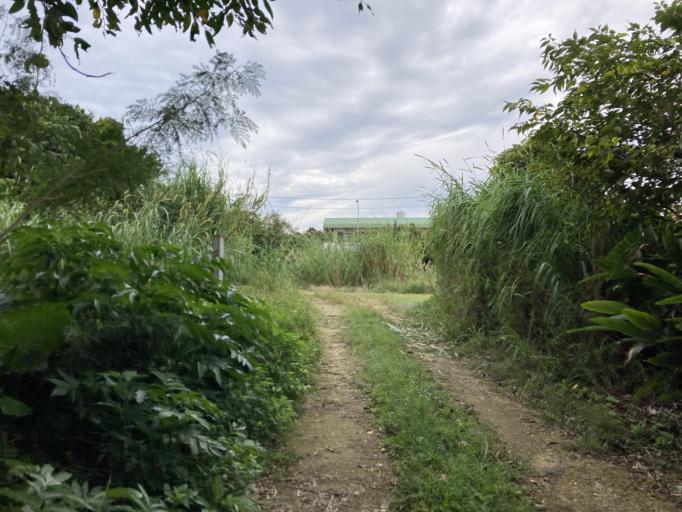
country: JP
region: Okinawa
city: Ishikawa
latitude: 26.3924
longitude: 127.7561
